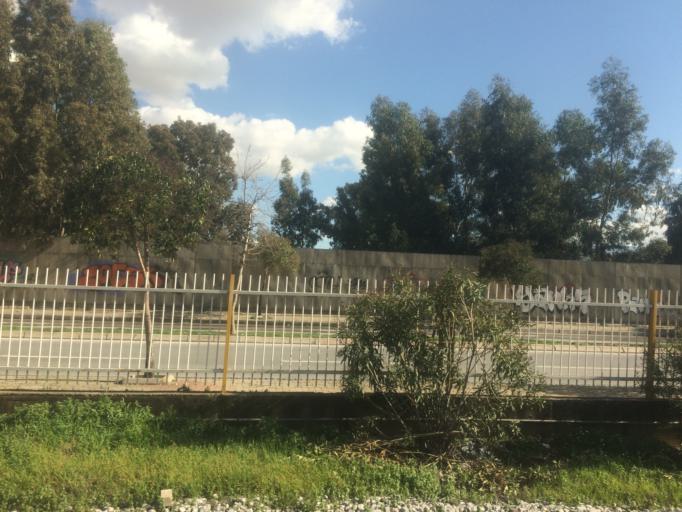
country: TR
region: Izmir
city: Buca
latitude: 38.4422
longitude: 27.1737
